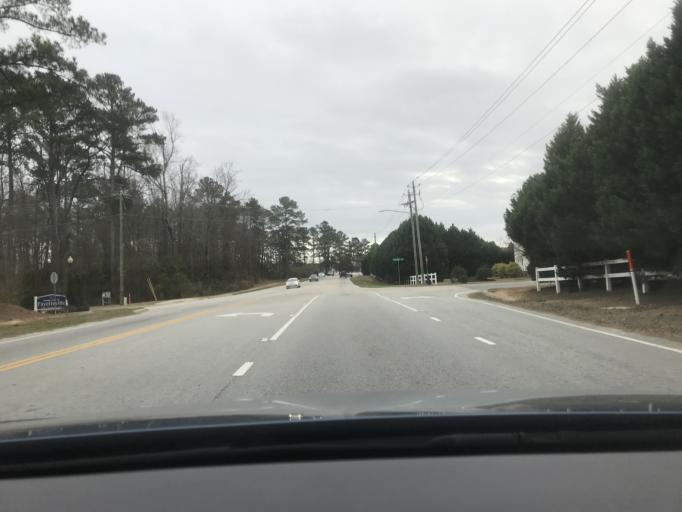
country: US
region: North Carolina
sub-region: Hoke County
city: Rockfish
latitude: 35.0471
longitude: -79.0091
